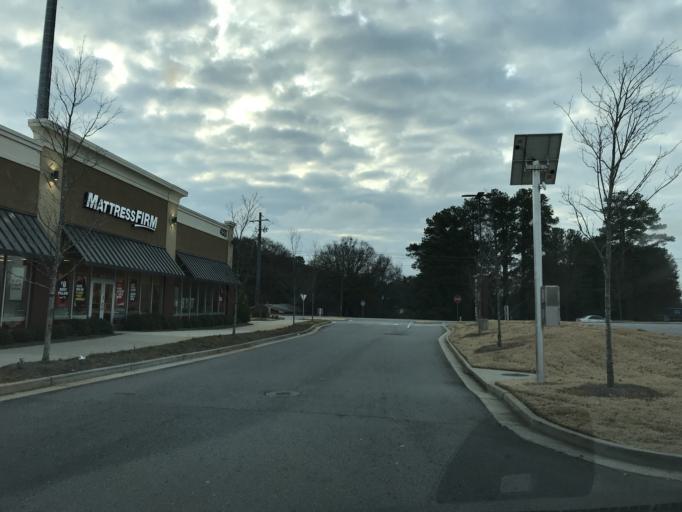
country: US
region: Georgia
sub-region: DeKalb County
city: Tucker
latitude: 33.8483
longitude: -84.2428
